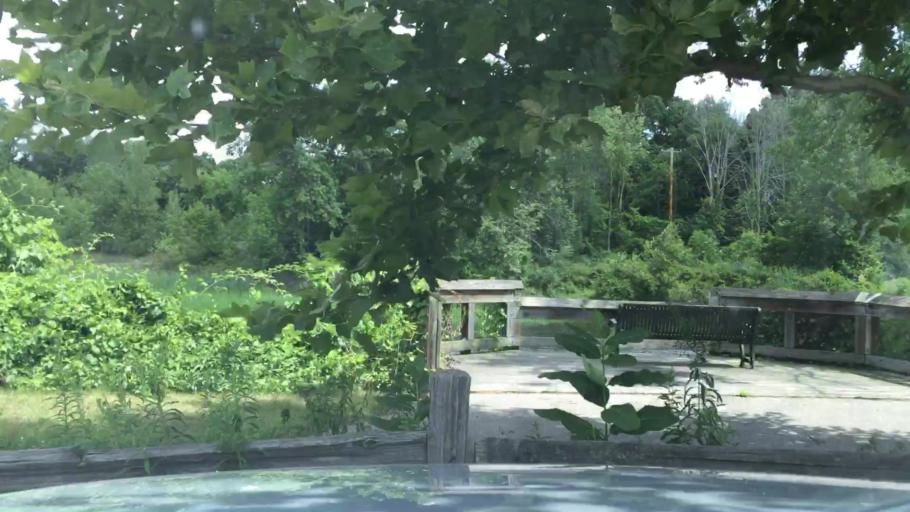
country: US
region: Michigan
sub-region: Ionia County
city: Belding
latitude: 43.0955
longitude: -85.2189
